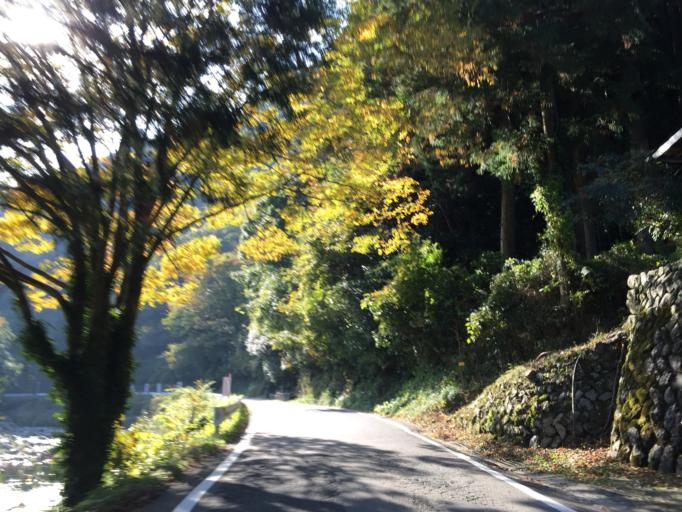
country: JP
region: Gifu
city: Minokamo
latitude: 35.5522
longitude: 137.1153
